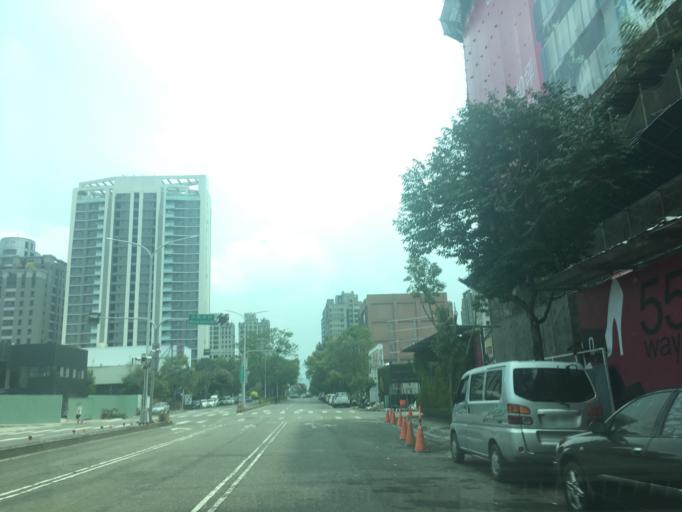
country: TW
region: Taiwan
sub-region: Taichung City
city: Taichung
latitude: 24.1859
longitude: 120.6834
